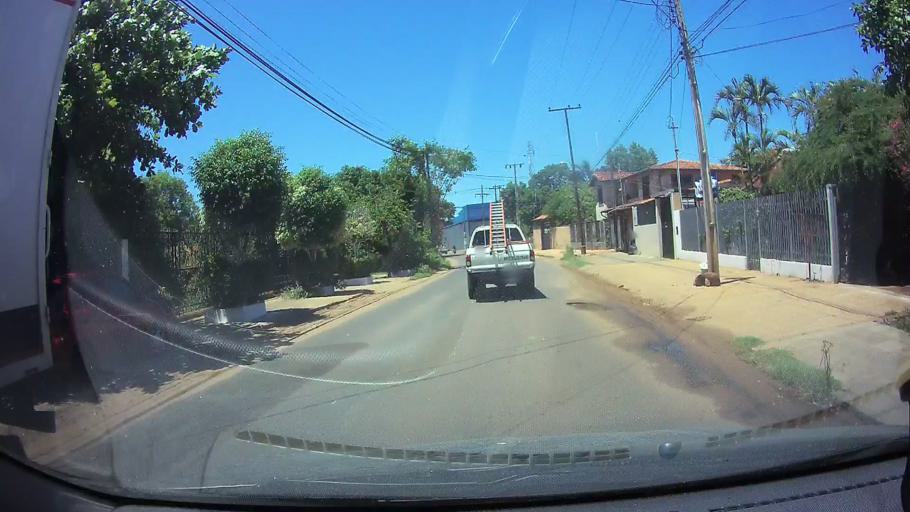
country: PY
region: Central
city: San Lorenzo
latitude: -25.3392
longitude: -57.4879
